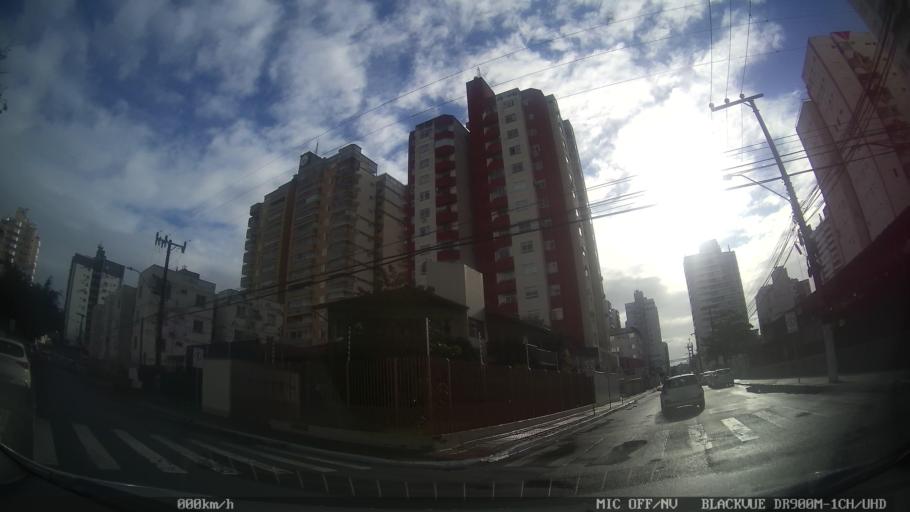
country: BR
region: Santa Catarina
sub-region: Sao Jose
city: Campinas
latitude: -27.5966
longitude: -48.6092
